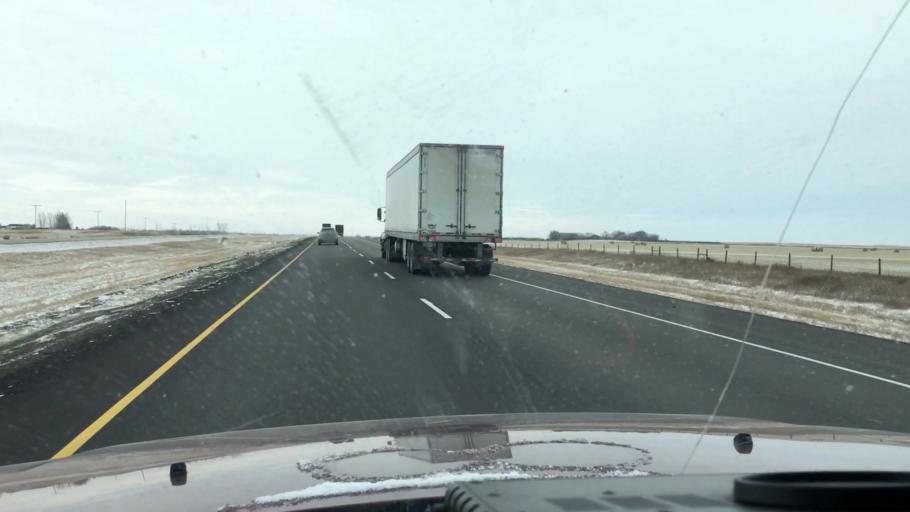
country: CA
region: Saskatchewan
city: Saskatoon
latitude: 51.7922
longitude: -106.4845
